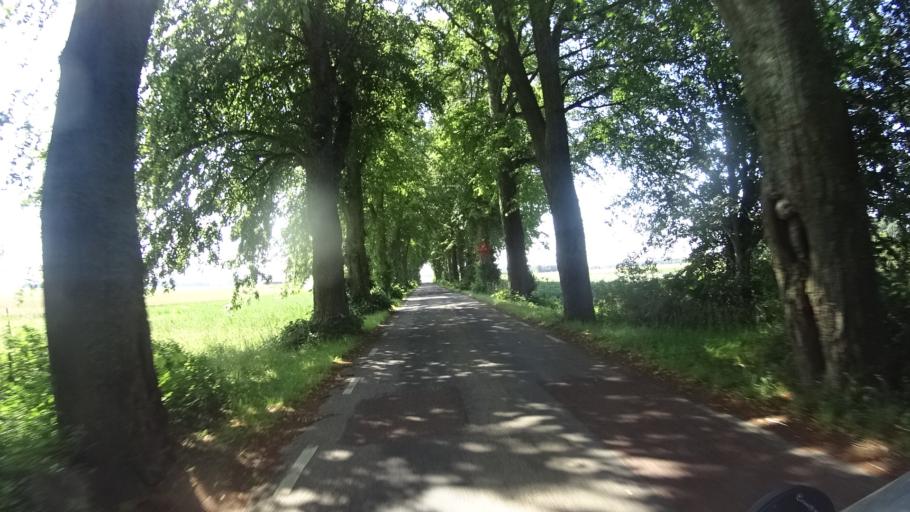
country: SE
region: OEstergoetland
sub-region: Vadstena Kommun
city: Herrestad
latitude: 58.3186
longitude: 14.8423
